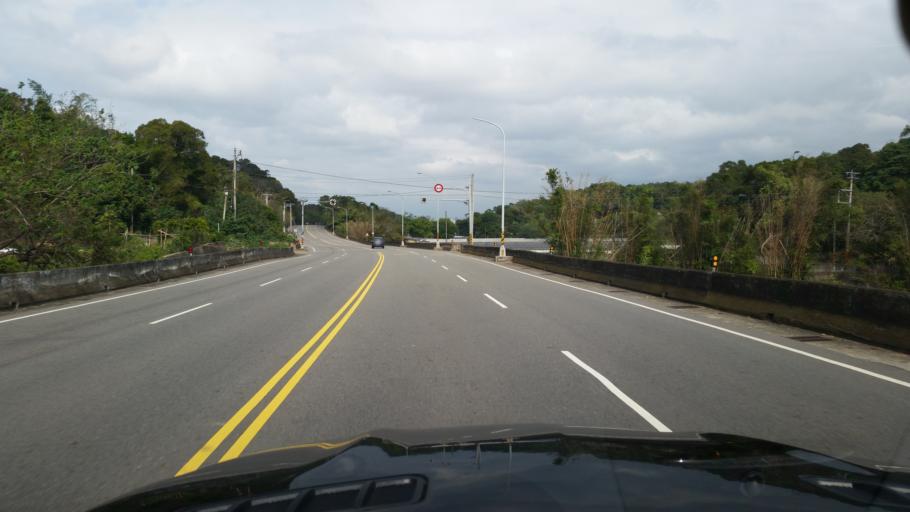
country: TW
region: Taiwan
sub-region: Miaoli
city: Miaoli
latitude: 24.6447
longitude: 120.8606
